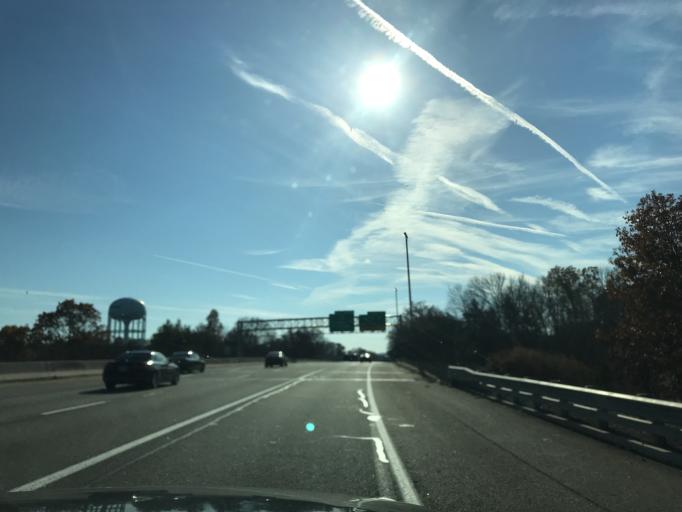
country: US
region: New Jersey
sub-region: Morris County
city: Parsippany
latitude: 40.8649
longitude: -74.4176
